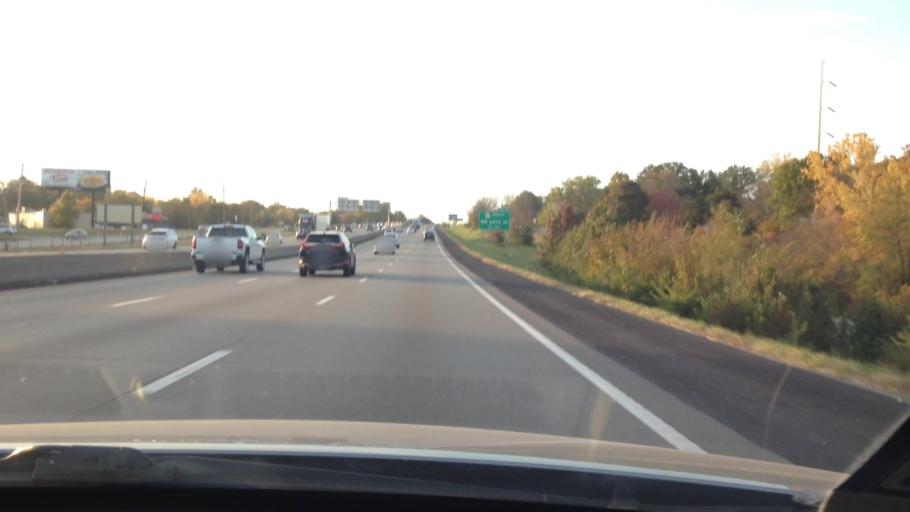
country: US
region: Missouri
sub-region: Platte County
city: Riverside
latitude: 39.2014
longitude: -94.6280
